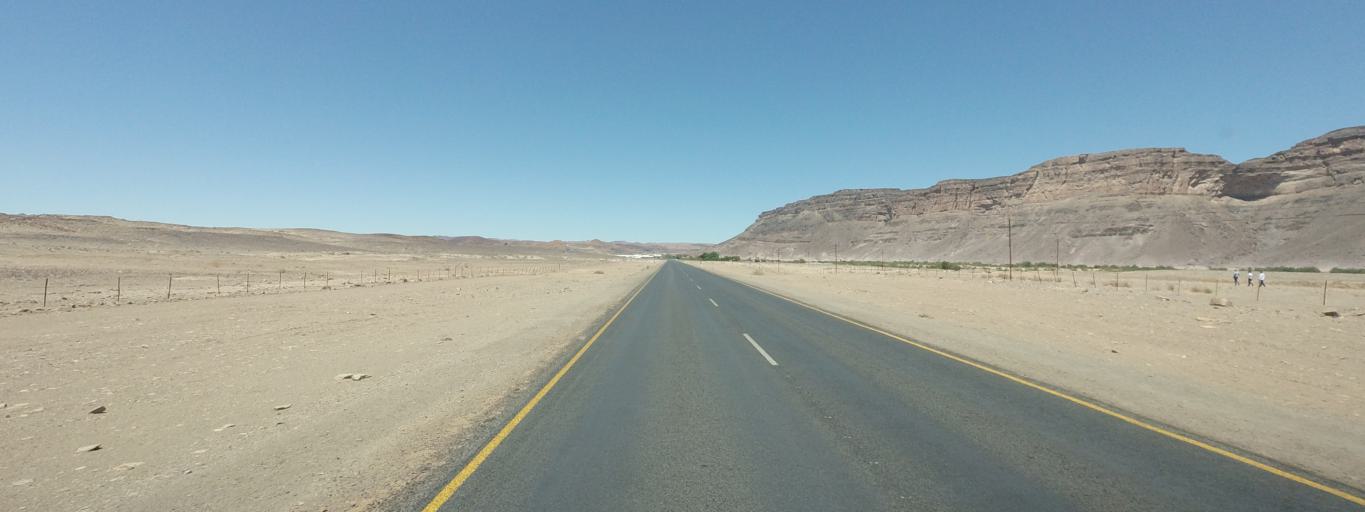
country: ZA
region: Northern Cape
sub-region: Namakwa District Municipality
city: Port Nolloth
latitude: -28.7477
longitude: 17.6184
